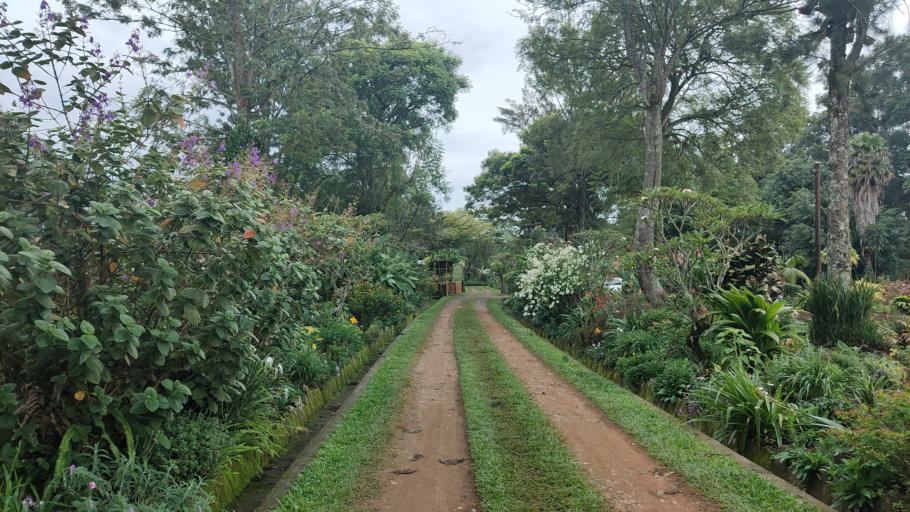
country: UG
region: Western Region
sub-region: Kabarole District
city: Fort Portal
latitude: 0.5945
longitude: 30.2498
